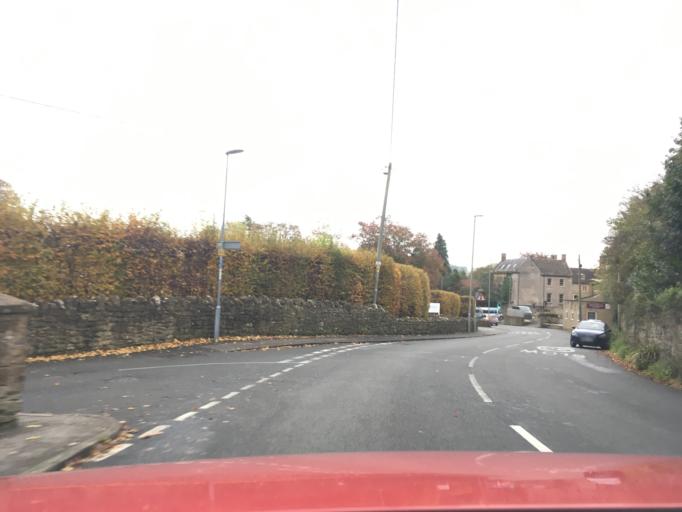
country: GB
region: England
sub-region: Dorset
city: Sherborne
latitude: 50.9513
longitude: -2.5221
